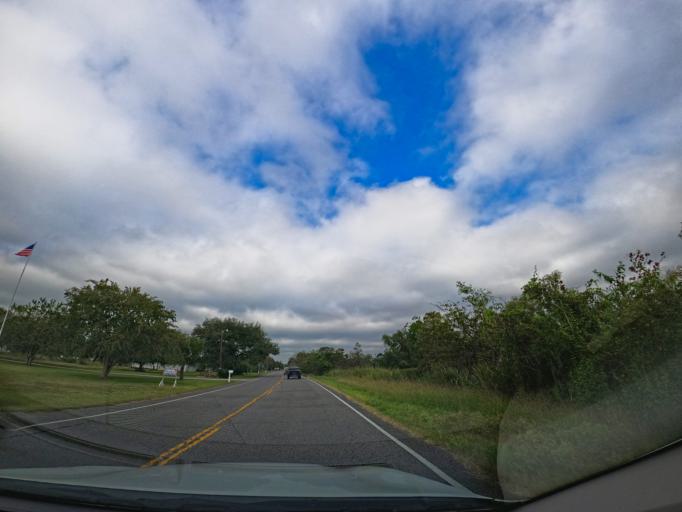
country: US
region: Louisiana
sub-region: Terrebonne Parish
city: Gray
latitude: 29.6164
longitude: -90.8977
